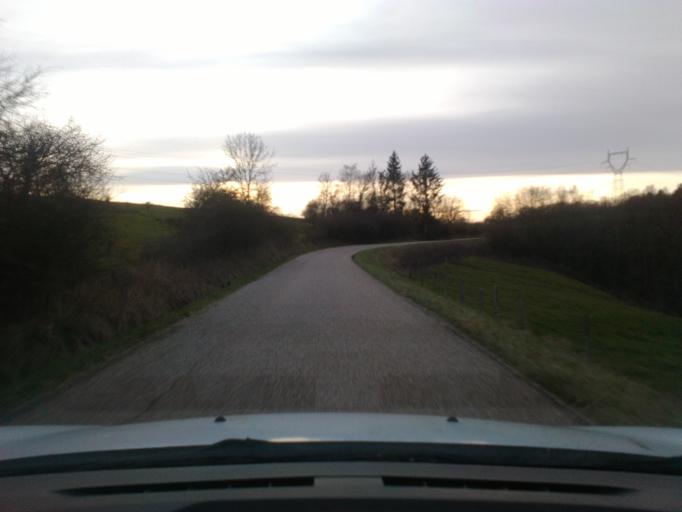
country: FR
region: Lorraine
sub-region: Departement des Vosges
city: Portieux
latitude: 48.3485
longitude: 6.3652
